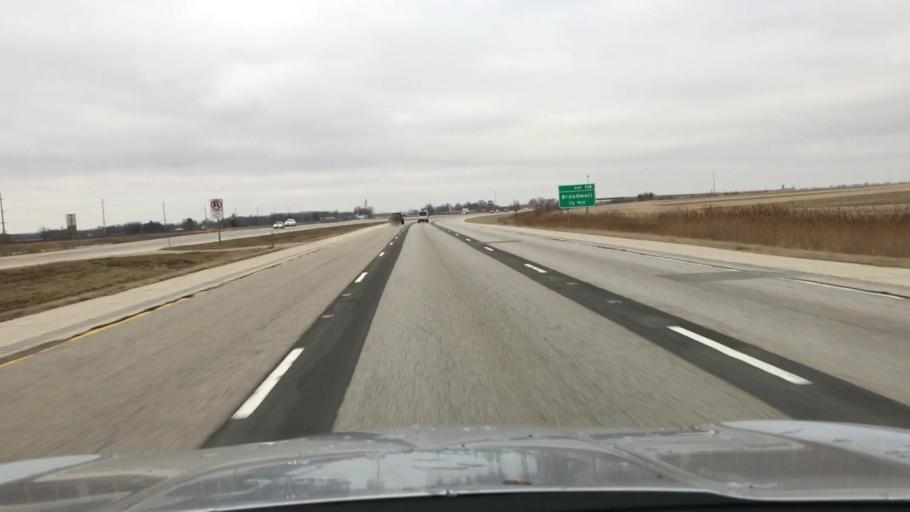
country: US
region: Illinois
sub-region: Logan County
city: Lincoln
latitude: 40.0819
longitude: -89.4325
